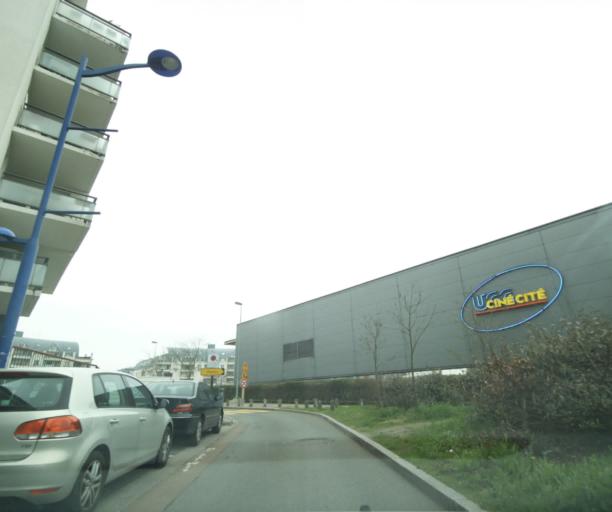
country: FR
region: Ile-de-France
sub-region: Departement du Val-d'Oise
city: Courdimanche
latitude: 49.0476
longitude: 2.0121
